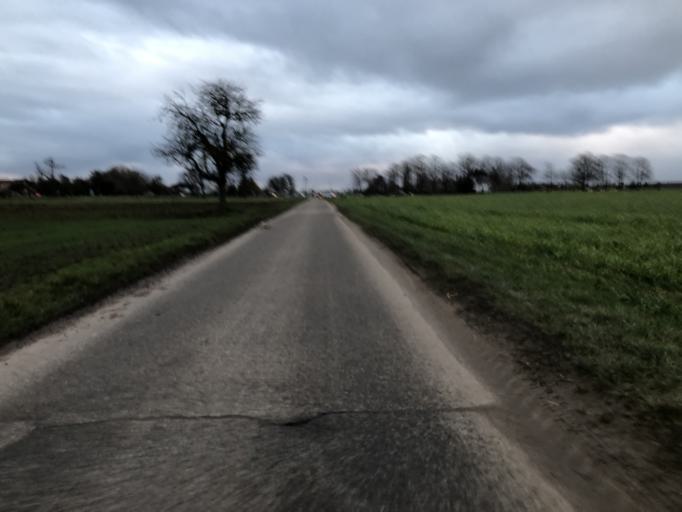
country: DE
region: Baden-Wuerttemberg
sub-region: Karlsruhe Region
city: Reilingen
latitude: 49.2928
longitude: 8.5834
